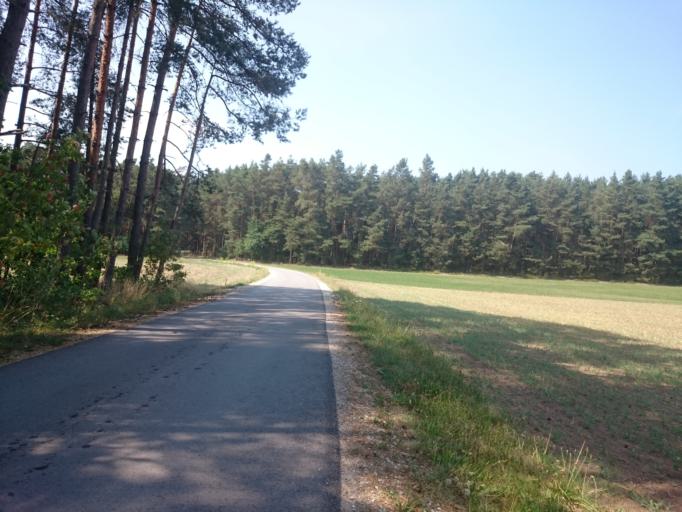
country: DE
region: Bavaria
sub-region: Regierungsbezirk Mittelfranken
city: Hilpoltstein
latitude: 49.1665
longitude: 11.1656
